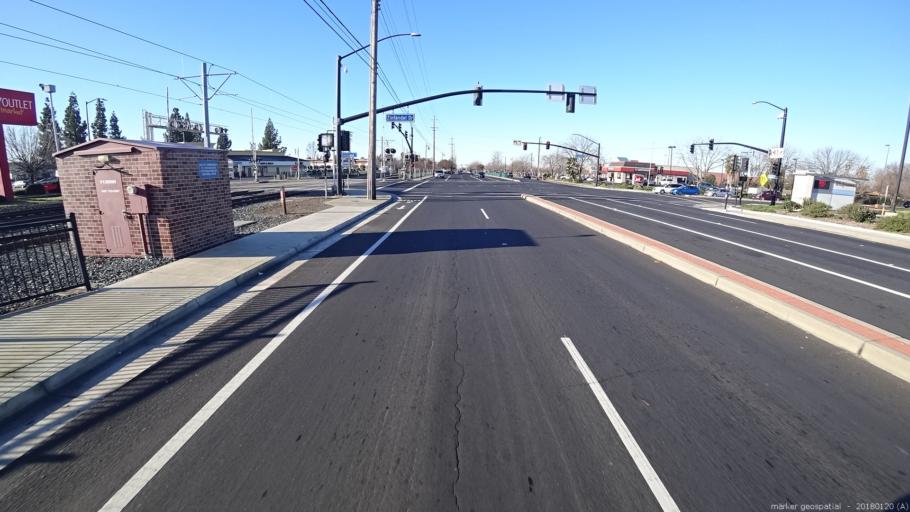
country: US
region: California
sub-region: Sacramento County
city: Rancho Cordova
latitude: 38.5962
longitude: -121.2885
